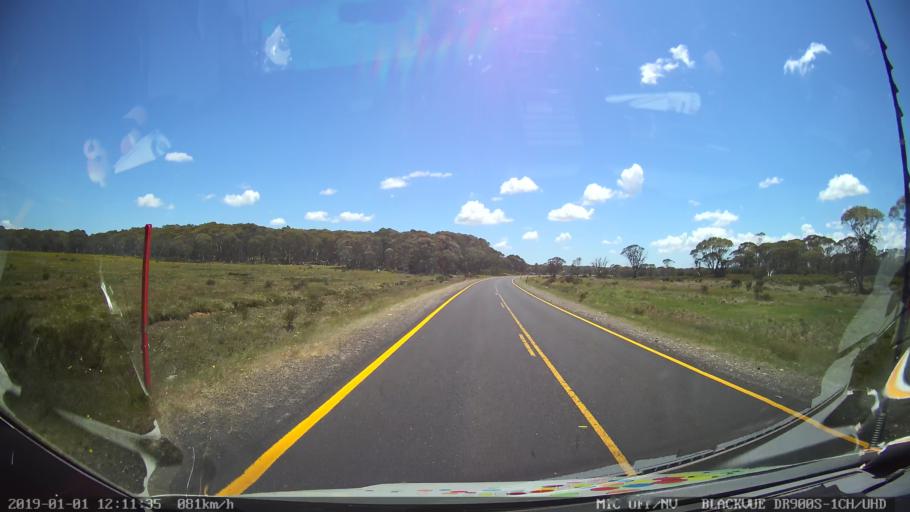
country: AU
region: New South Wales
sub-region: Tumut Shire
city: Tumut
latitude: -35.7825
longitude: 148.5083
